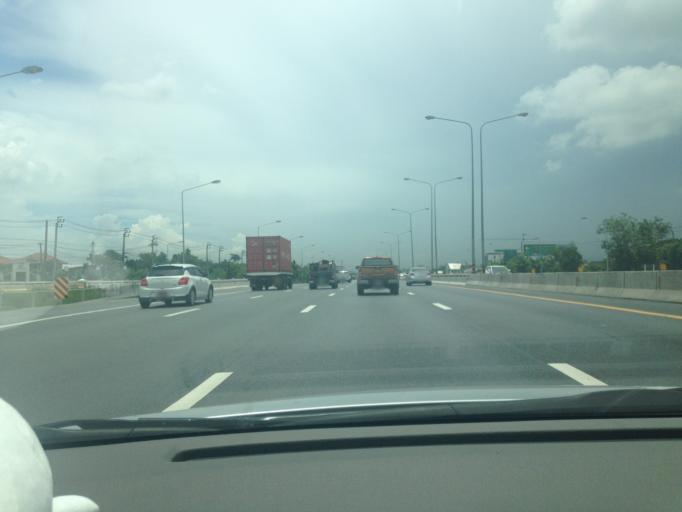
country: TH
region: Bangkok
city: Suan Luang
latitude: 13.7016
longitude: 100.6995
